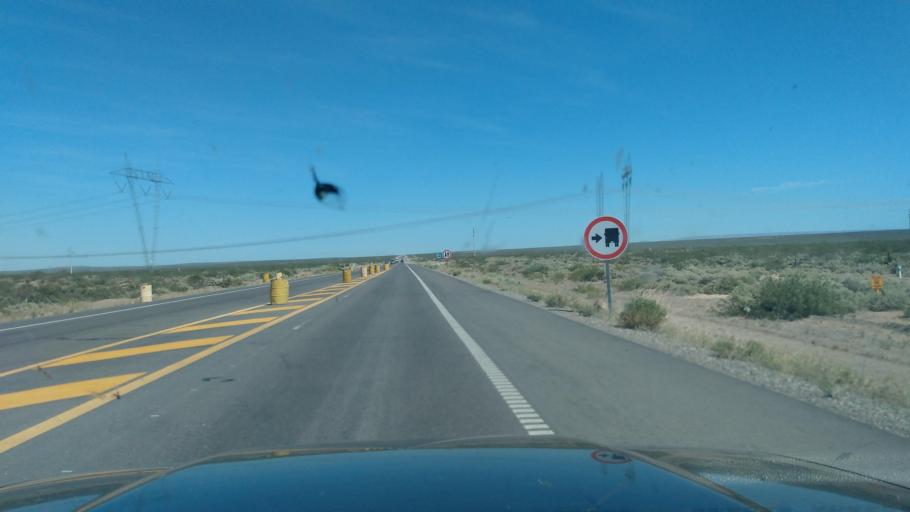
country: AR
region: Neuquen
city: Senillosa
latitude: -39.0750
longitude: -68.5975
